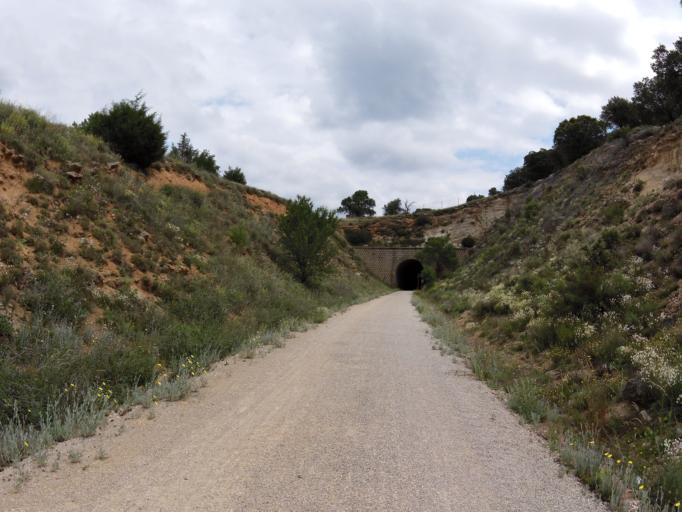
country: ES
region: Castille-La Mancha
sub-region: Provincia de Albacete
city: Robledo
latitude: 38.7808
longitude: -2.3878
